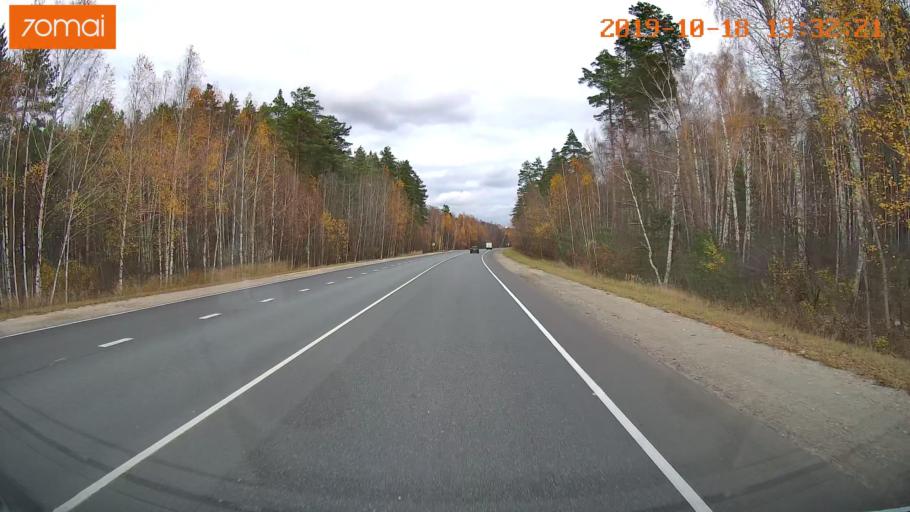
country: RU
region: Rjazan
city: Solotcha
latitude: 54.8320
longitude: 39.9173
